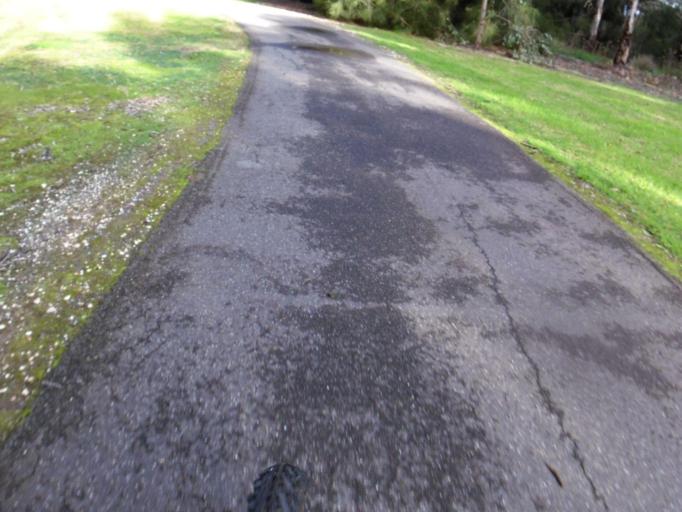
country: AU
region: Victoria
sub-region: Greater Geelong
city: Breakwater
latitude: -38.1788
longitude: 144.3633
